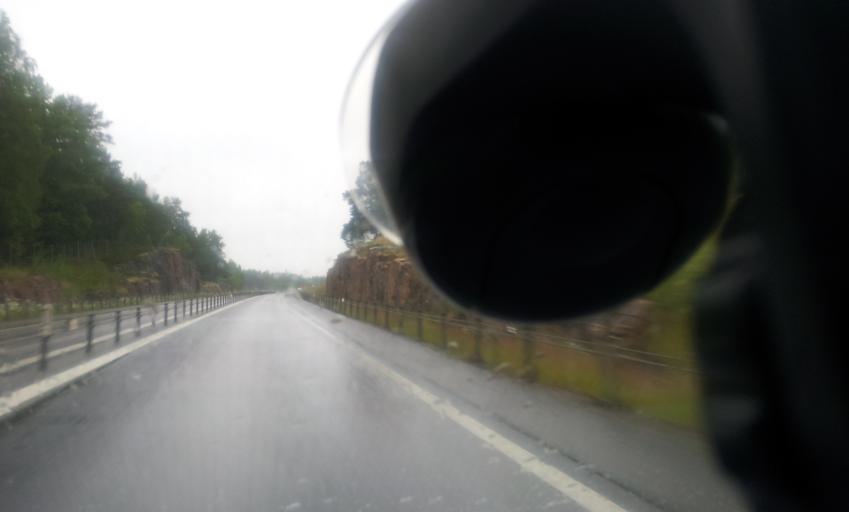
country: SE
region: OEstergoetland
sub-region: Valdemarsviks Kommun
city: Gusum
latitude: 58.3640
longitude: 16.4339
